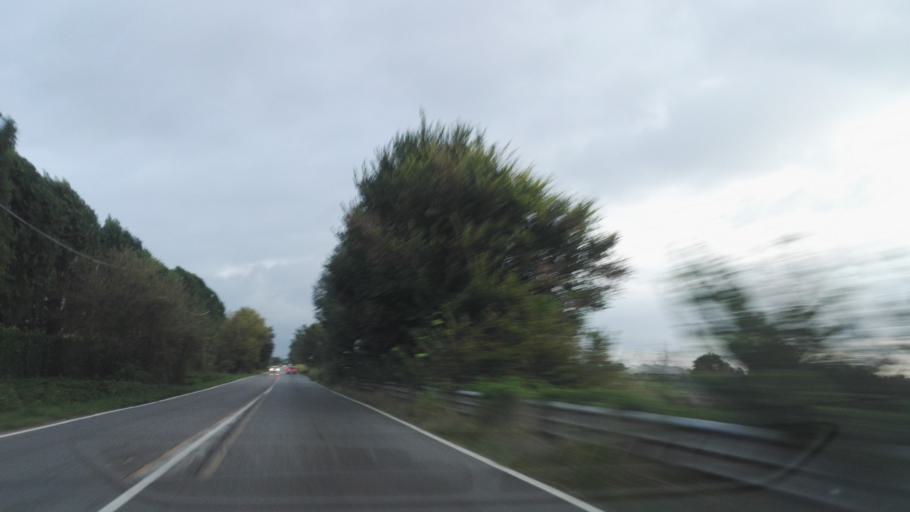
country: IT
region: Lombardy
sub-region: Citta metropolitana di Milano
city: Settala
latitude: 45.4441
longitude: 9.3883
